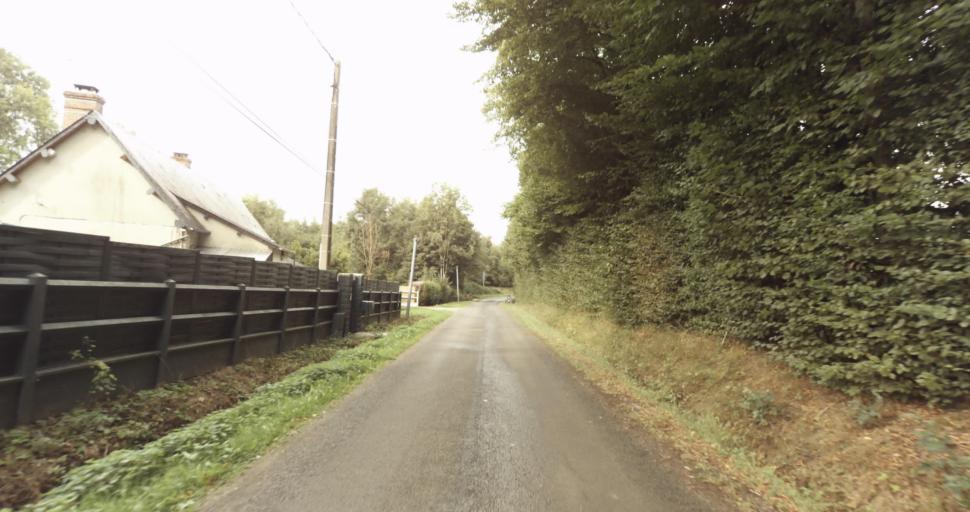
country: FR
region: Lower Normandy
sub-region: Departement de l'Orne
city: Sainte-Gauburge-Sainte-Colombe
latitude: 48.7067
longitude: 0.3709
